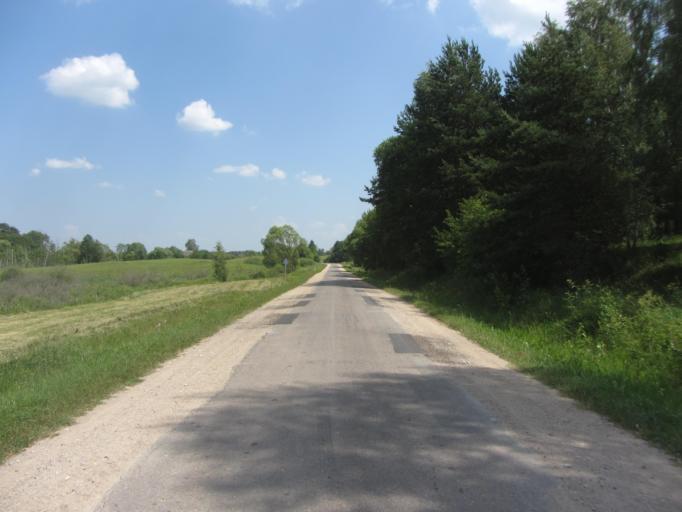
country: LT
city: Lazdijai
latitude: 54.2276
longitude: 23.4274
